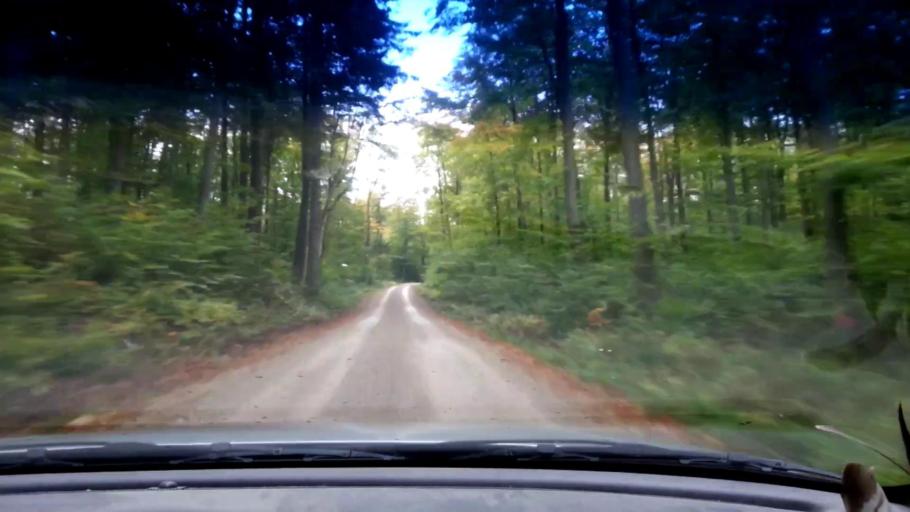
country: DE
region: Bavaria
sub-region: Upper Franconia
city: Litzendorf
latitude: 49.8958
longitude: 11.0652
